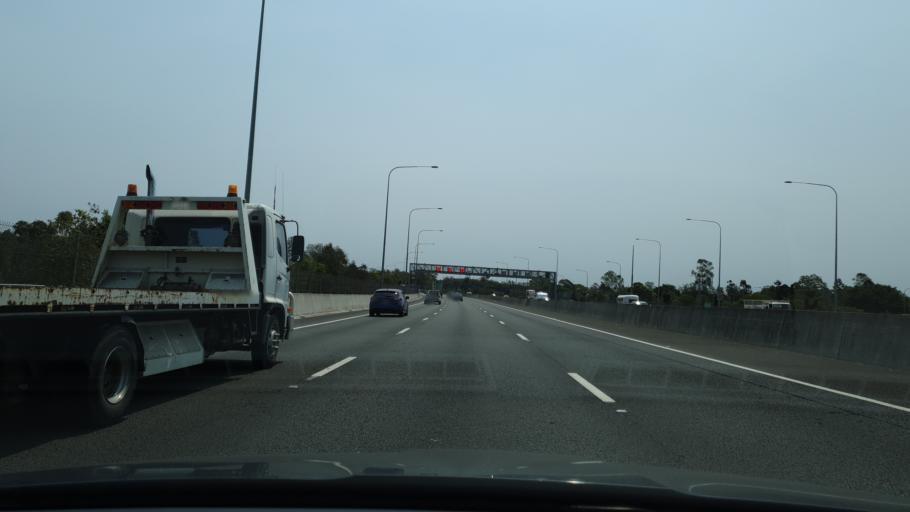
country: AU
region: Queensland
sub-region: Ipswich
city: Redbank
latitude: -27.6012
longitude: 152.8789
